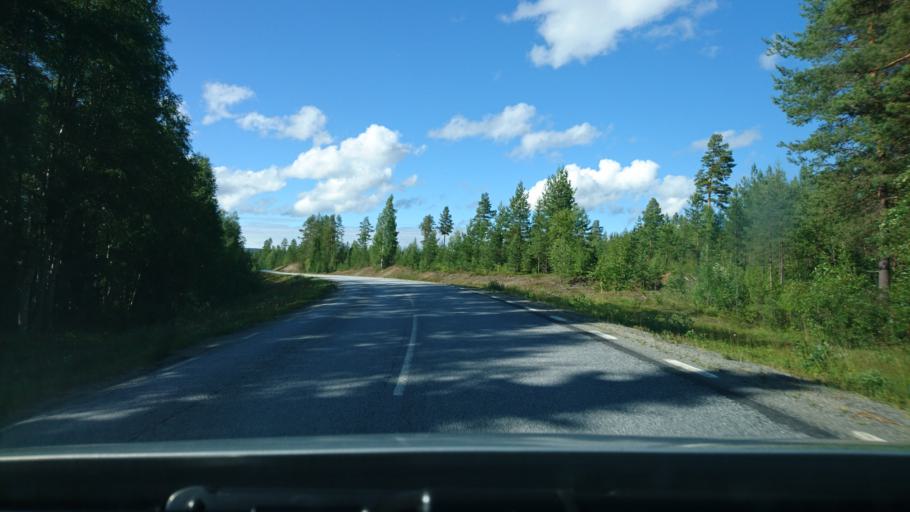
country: SE
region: Vaesterbotten
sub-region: Asele Kommun
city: Asele
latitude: 64.2413
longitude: 17.2946
